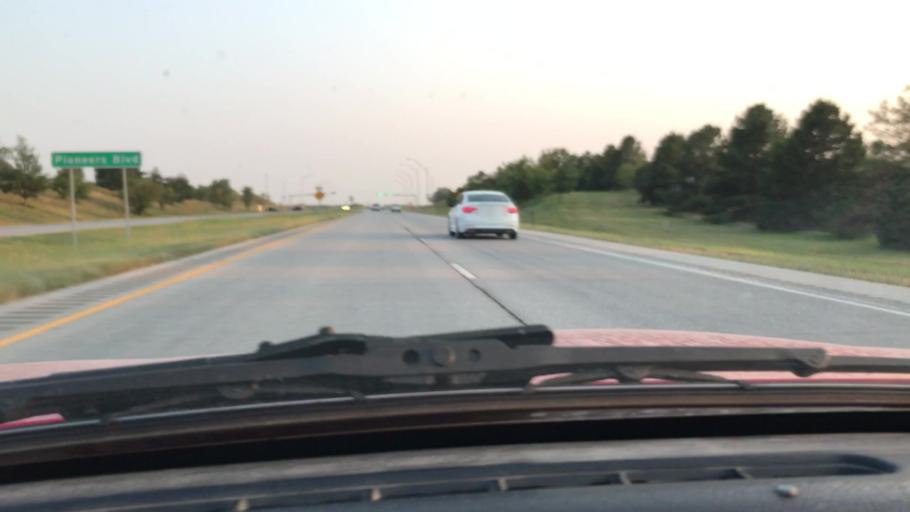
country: US
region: Nebraska
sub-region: Lancaster County
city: Lincoln
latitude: 40.7731
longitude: -96.7274
